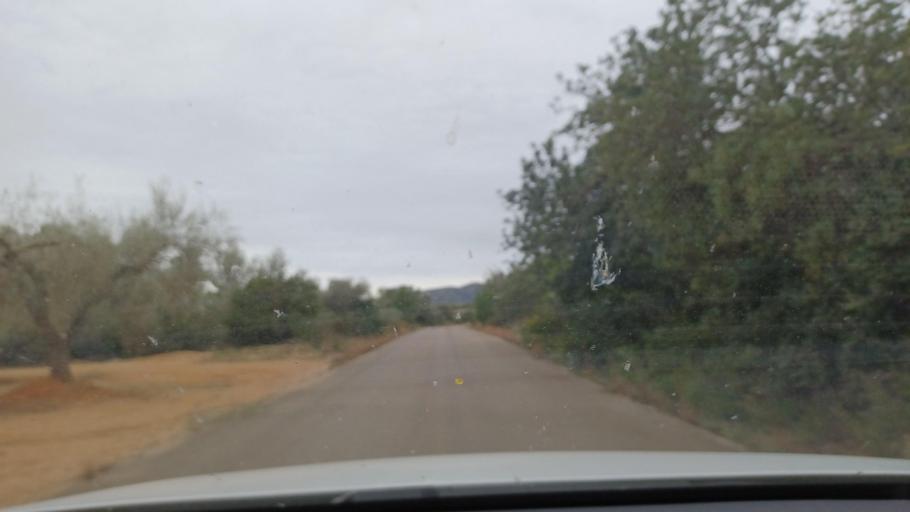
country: ES
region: Valencia
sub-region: Provincia de Castello
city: Canet lo Roig
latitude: 40.5837
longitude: 0.2843
